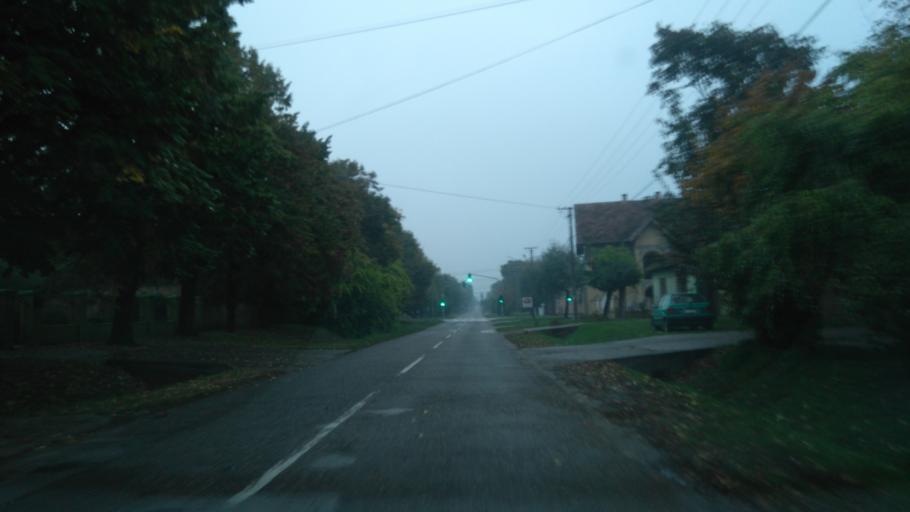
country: RS
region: Autonomna Pokrajina Vojvodina
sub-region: Juznobacki Okrug
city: Becej
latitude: 45.6126
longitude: 20.0368
